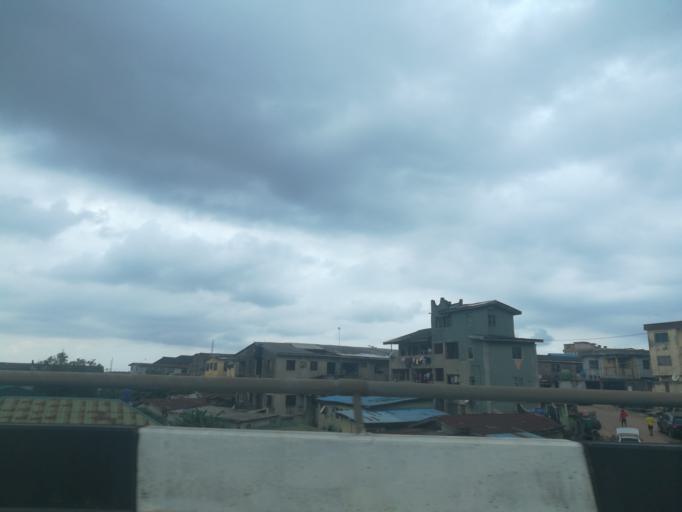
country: NG
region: Lagos
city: Somolu
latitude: 6.5500
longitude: 3.3954
